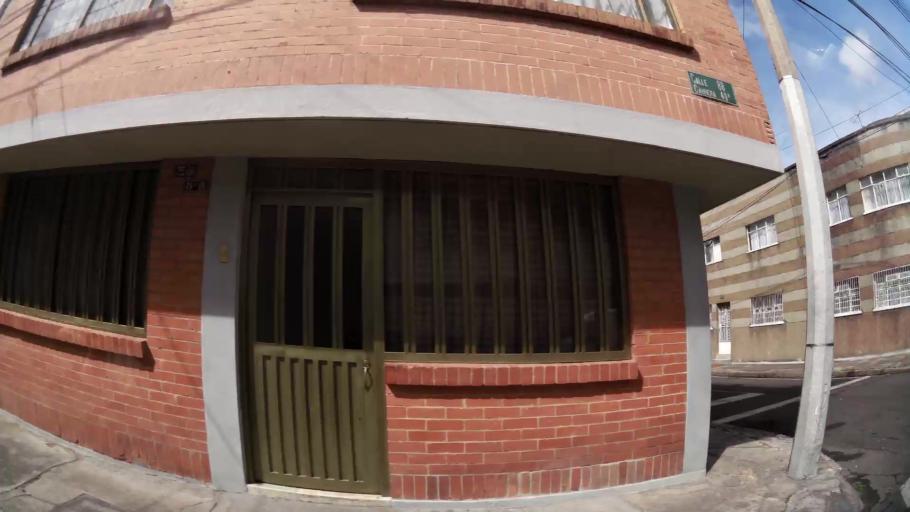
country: CO
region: Bogota D.C.
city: Barrio San Luis
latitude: 4.6782
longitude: -74.0642
